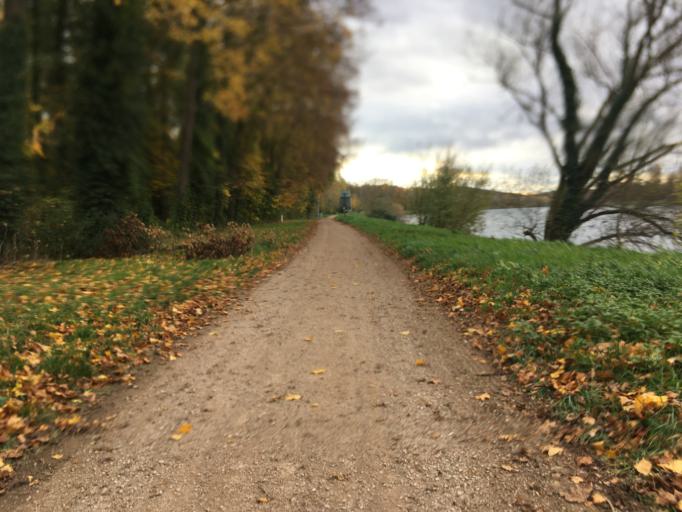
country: DE
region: Baden-Wuerttemberg
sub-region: Freiburg Region
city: Sasbach
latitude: 48.1438
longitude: 7.6018
